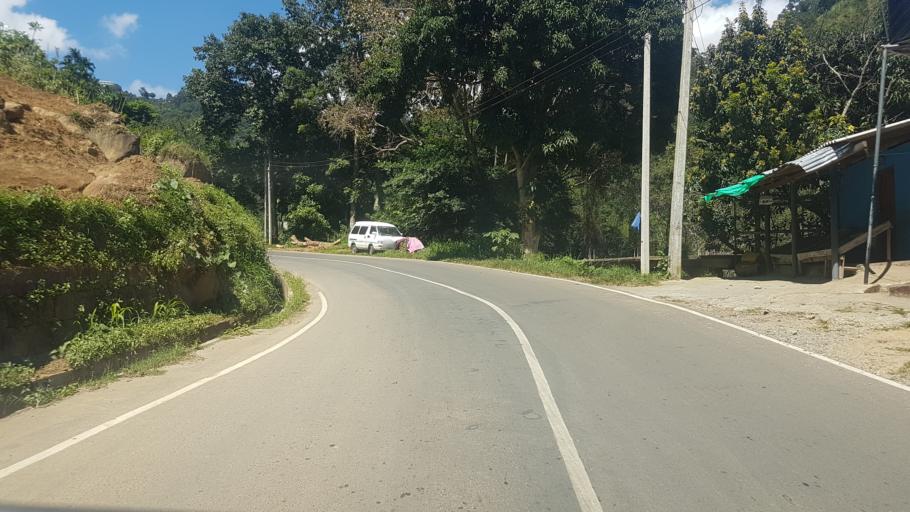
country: LK
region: Uva
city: Badulla
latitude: 6.8659
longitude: 81.0518
